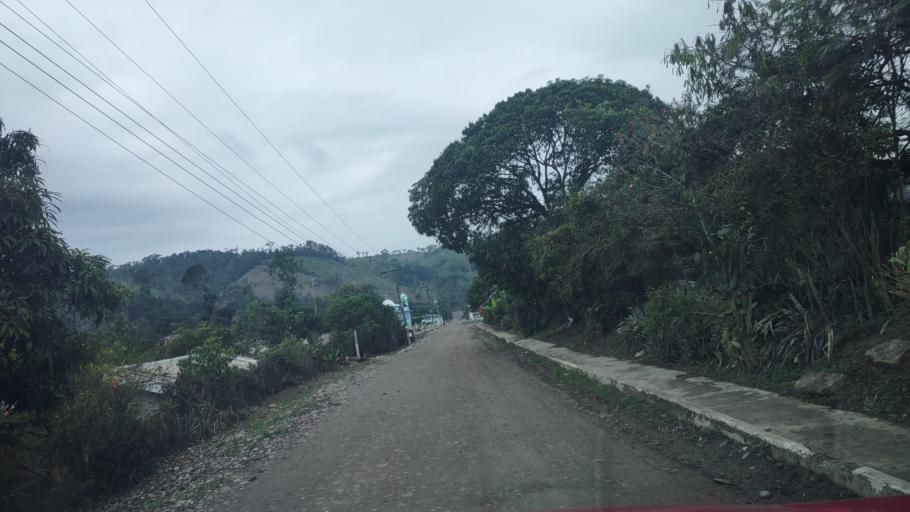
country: MX
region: Veracruz
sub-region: Coatzintla
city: Manuel Maria Contreras
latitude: 20.4001
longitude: -97.4388
